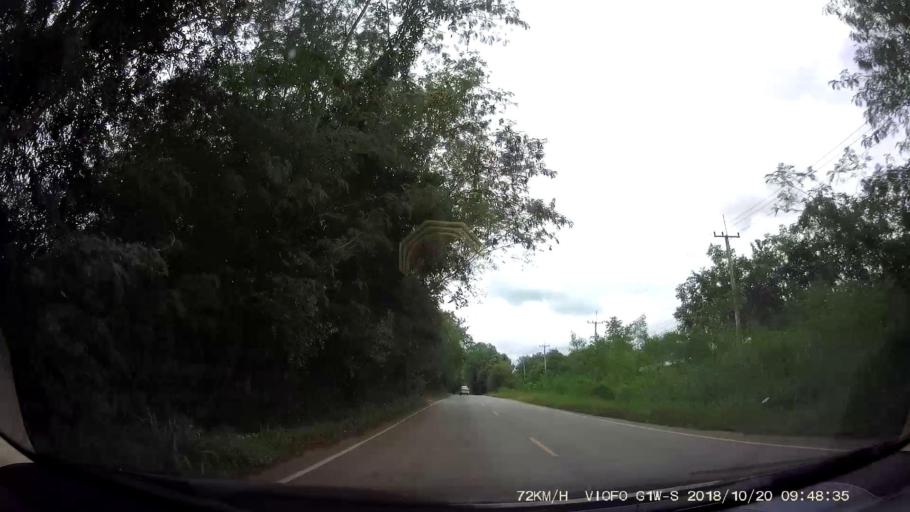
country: TH
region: Chaiyaphum
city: Khon San
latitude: 16.5124
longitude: 101.9109
